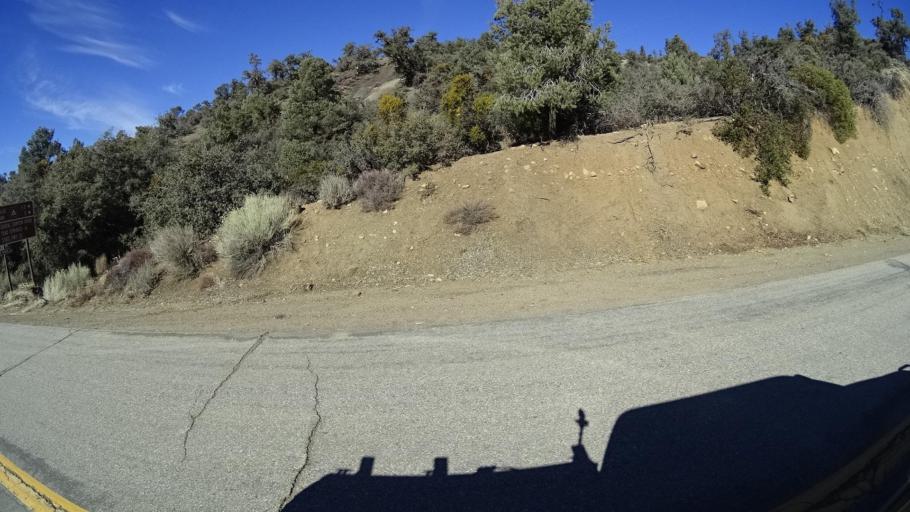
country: US
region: California
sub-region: Kern County
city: Pine Mountain Club
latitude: 34.8634
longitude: -119.2268
